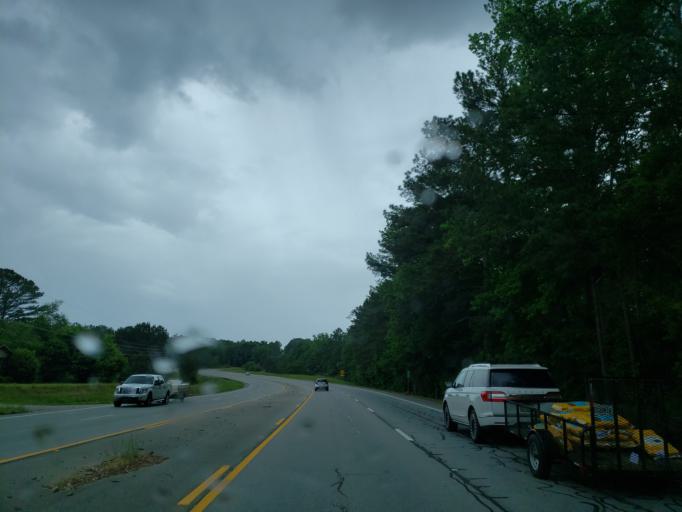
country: US
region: Georgia
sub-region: Haralson County
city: Buchanan
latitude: 33.8203
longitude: -85.2037
